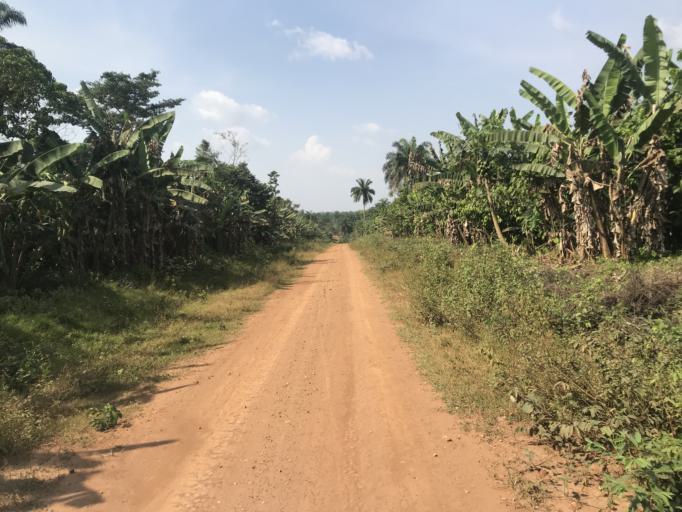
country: NG
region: Osun
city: Osu
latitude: 7.6374
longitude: 4.6601
